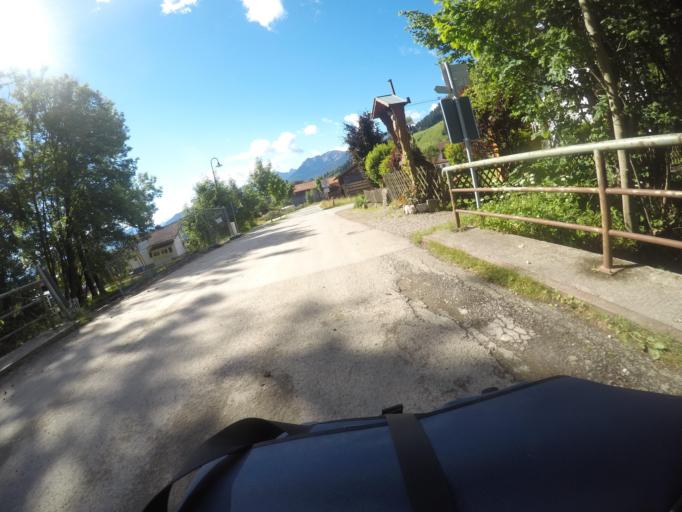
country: DE
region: Bavaria
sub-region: Swabia
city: Pfronten
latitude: 47.6069
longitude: 10.5341
